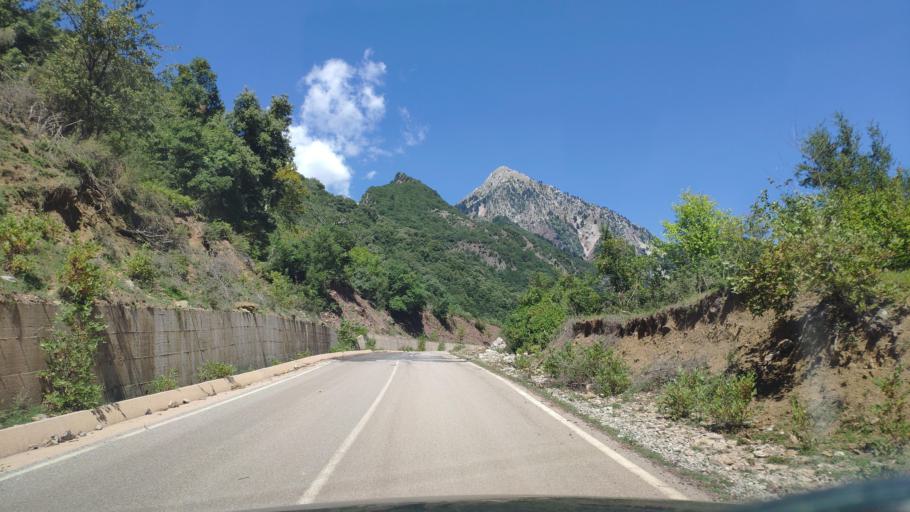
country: GR
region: Central Greece
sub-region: Nomos Evrytanias
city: Kerasochori
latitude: 39.0753
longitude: 21.5981
